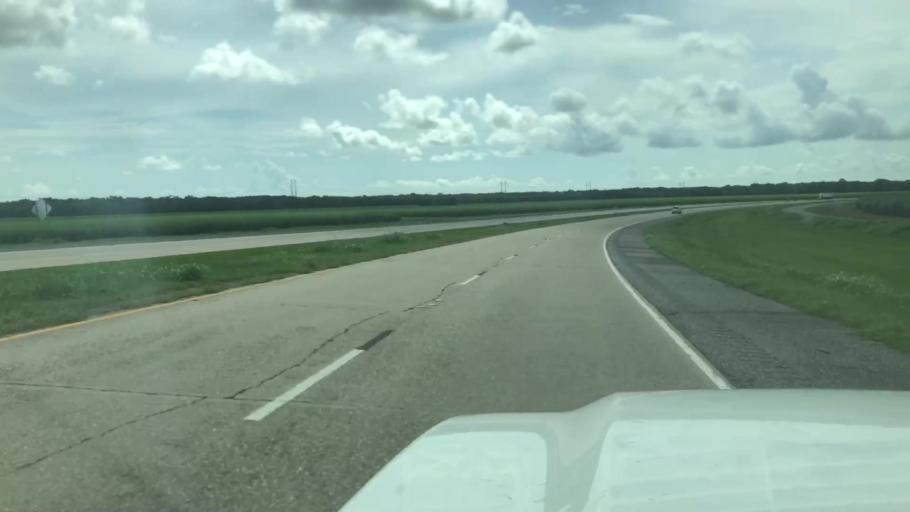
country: US
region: Louisiana
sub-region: Saint Mary Parish
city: Franklin
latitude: 29.7576
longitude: -91.4692
